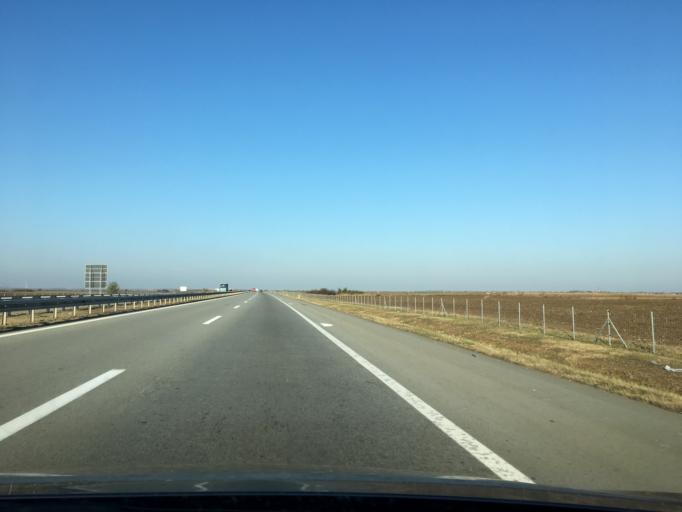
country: RS
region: Autonomna Pokrajina Vojvodina
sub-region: Juznobacki Okrug
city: Kovilj
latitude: 45.2521
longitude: 20.0164
